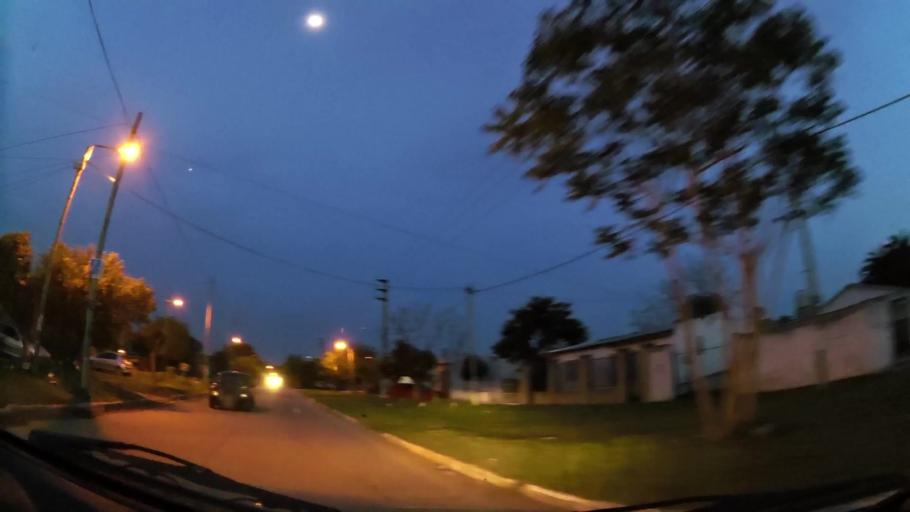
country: AR
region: Buenos Aires
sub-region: Partido de Almirante Brown
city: Adrogue
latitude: -34.8076
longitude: -58.2943
